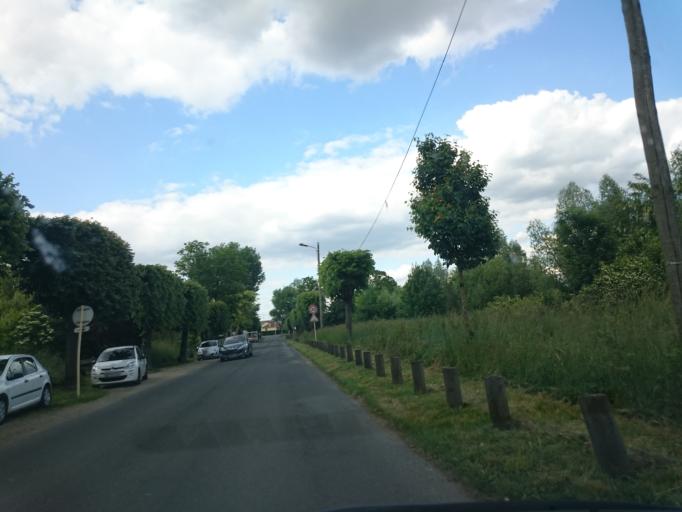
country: FR
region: Ile-de-France
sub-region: Departement de l'Essonne
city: Viry-Chatillon
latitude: 48.6657
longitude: 2.3935
